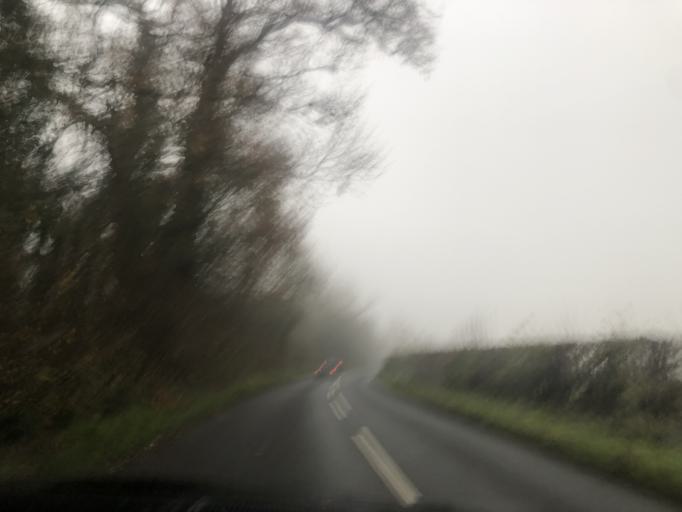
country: GB
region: England
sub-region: Oxfordshire
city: Bicester
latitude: 51.9224
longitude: -1.1854
